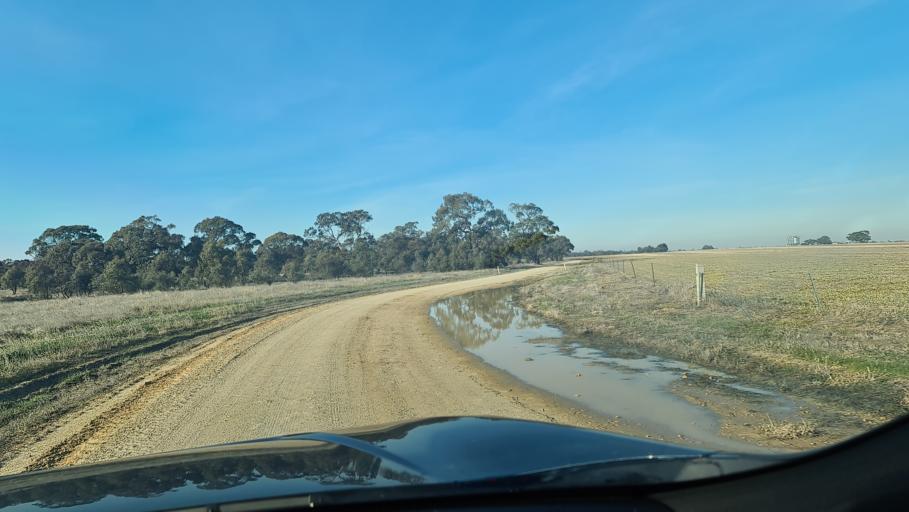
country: AU
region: Victoria
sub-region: Horsham
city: Horsham
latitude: -36.3567
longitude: 142.3963
